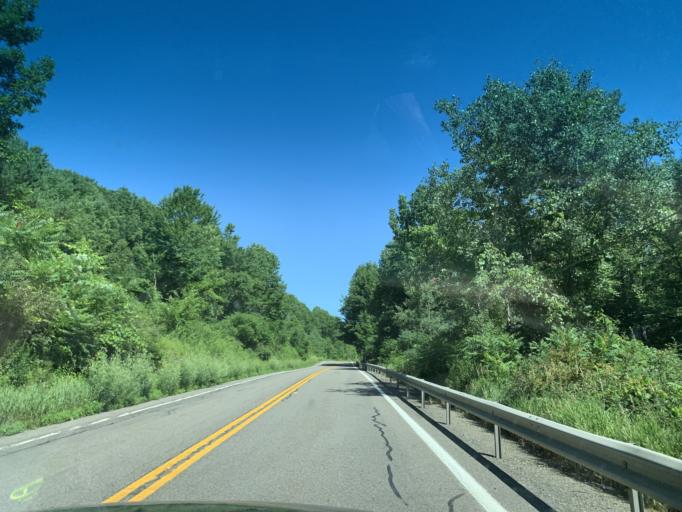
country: US
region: New York
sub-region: Chenango County
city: Norwich
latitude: 42.4761
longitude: -75.4040
